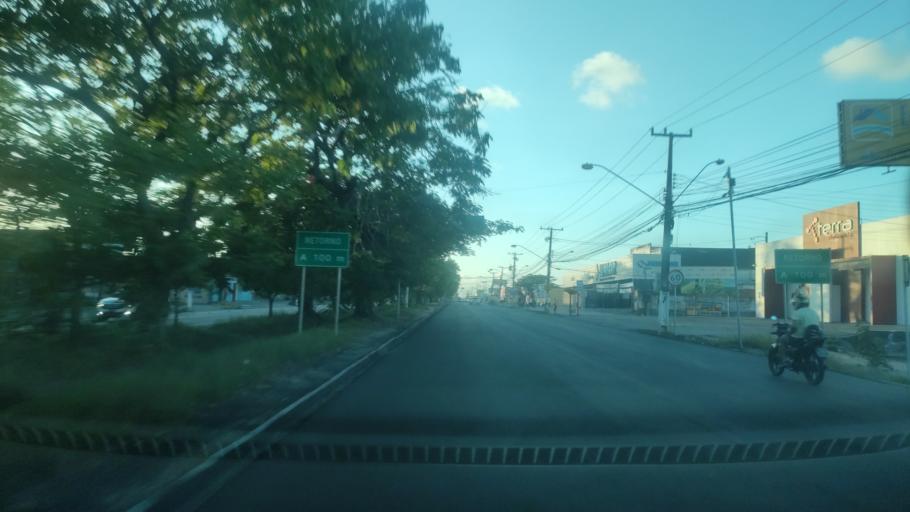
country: BR
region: Alagoas
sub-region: Satuba
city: Satuba
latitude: -9.5786
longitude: -35.7689
